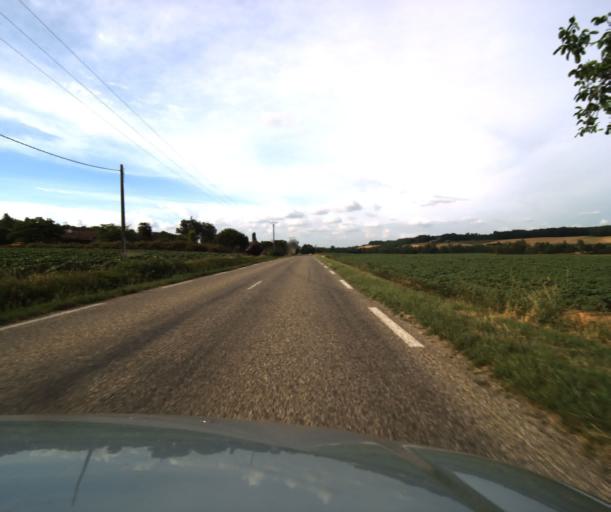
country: FR
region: Midi-Pyrenees
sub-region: Departement du Tarn-et-Garonne
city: Beaumont-de-Lomagne
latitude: 43.7851
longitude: 0.8912
